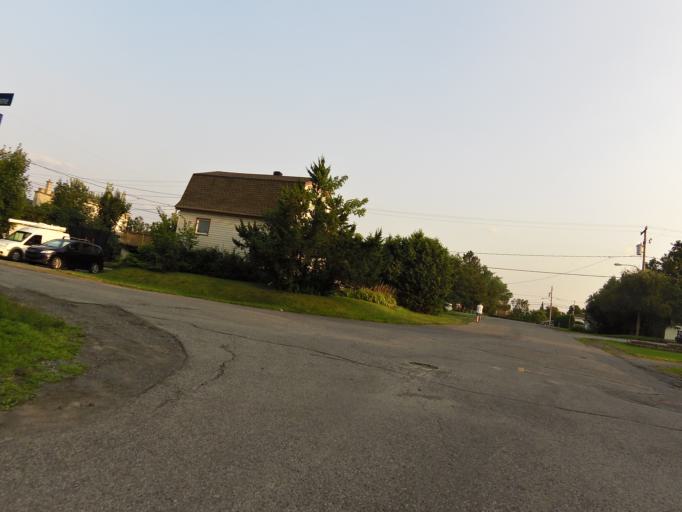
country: CA
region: Ontario
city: Bells Corners
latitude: 45.3855
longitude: -75.8031
